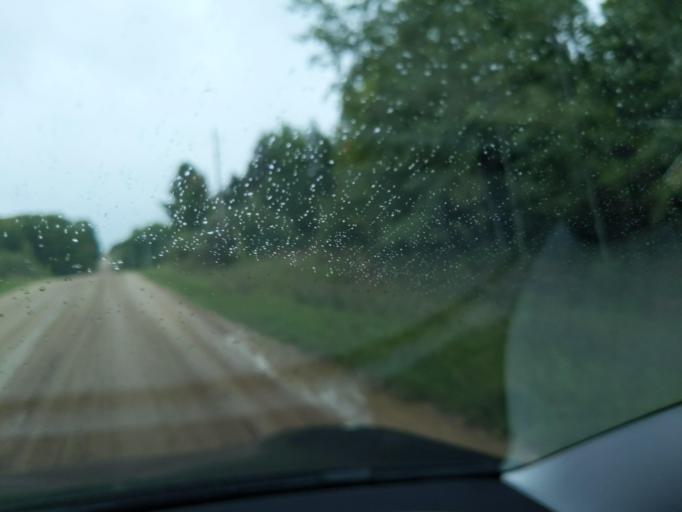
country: US
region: Michigan
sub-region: Antrim County
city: Elk Rapids
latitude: 44.8165
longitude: -85.3944
